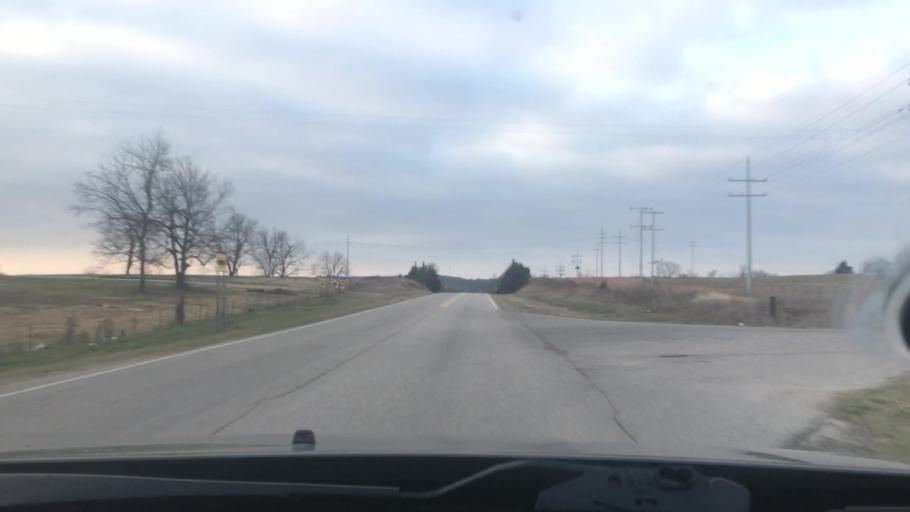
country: US
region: Oklahoma
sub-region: Pontotoc County
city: Ada
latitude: 34.6222
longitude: -96.6349
